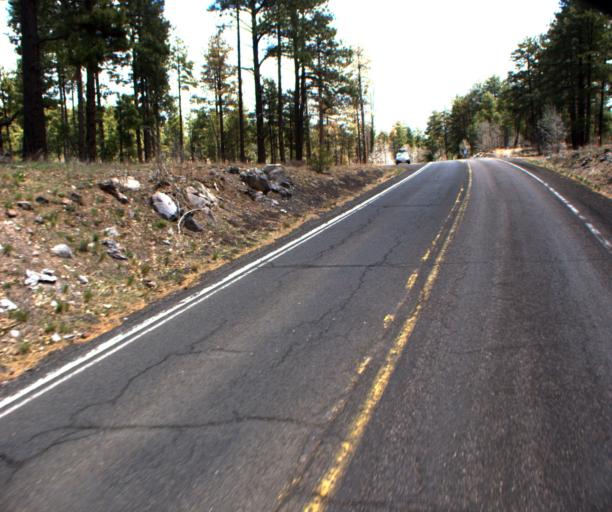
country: US
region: Arizona
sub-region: Coconino County
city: Kachina Village
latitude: 35.1093
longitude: -111.7191
